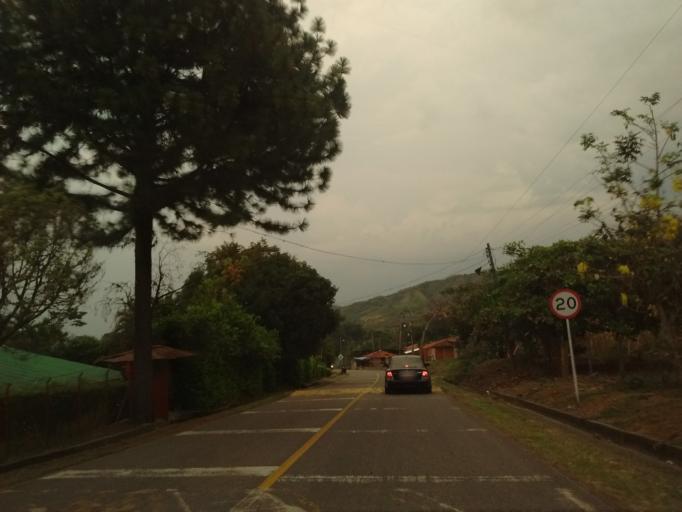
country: CO
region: Cauca
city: Caloto
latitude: 3.0722
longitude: -76.3527
